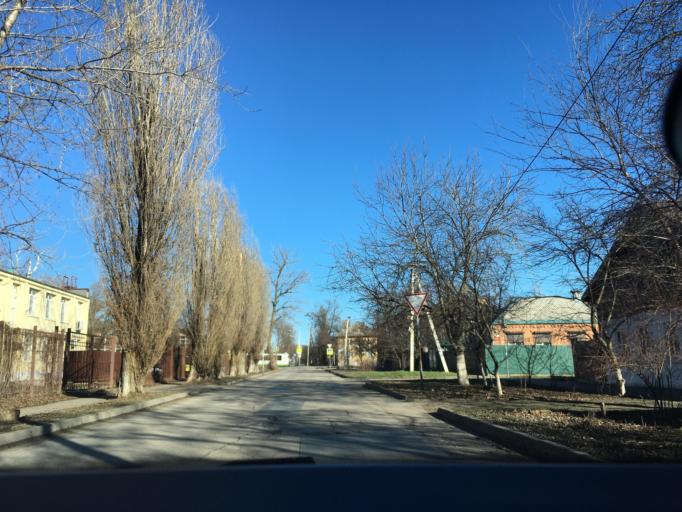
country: RU
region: Rostov
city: Imeni Chkalova
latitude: 47.2695
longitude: 39.7920
